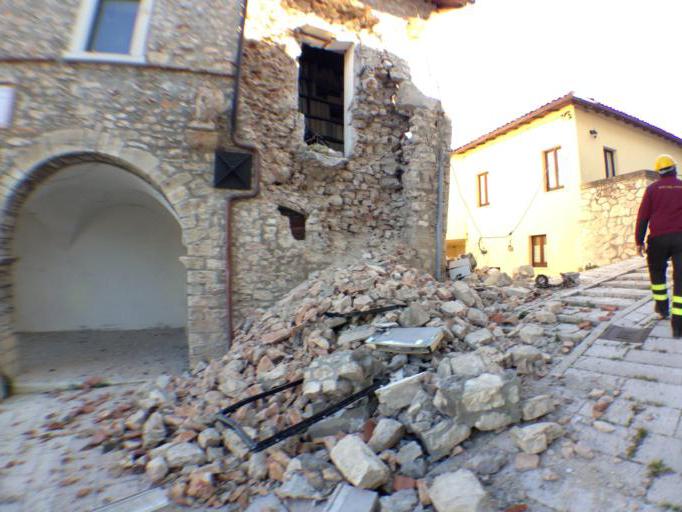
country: IT
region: Umbria
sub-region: Provincia di Perugia
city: Preci
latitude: 42.8791
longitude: 13.0391
